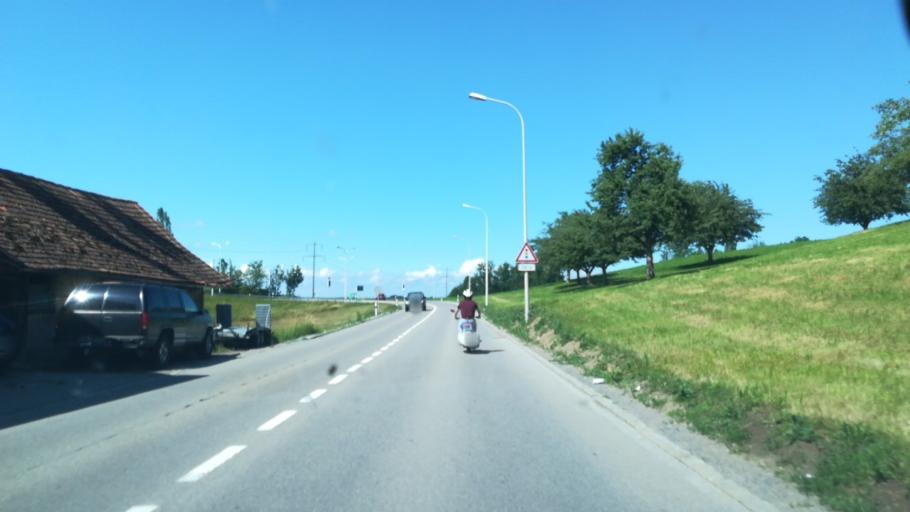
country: CH
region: Saint Gallen
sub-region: Wahlkreis St. Gallen
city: Gossau
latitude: 47.4305
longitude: 9.2439
